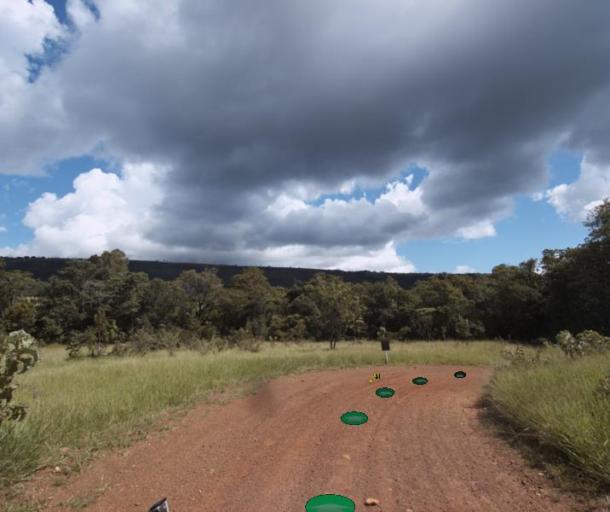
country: BR
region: Goias
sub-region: Pirenopolis
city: Pirenopolis
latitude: -15.7884
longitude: -48.8712
